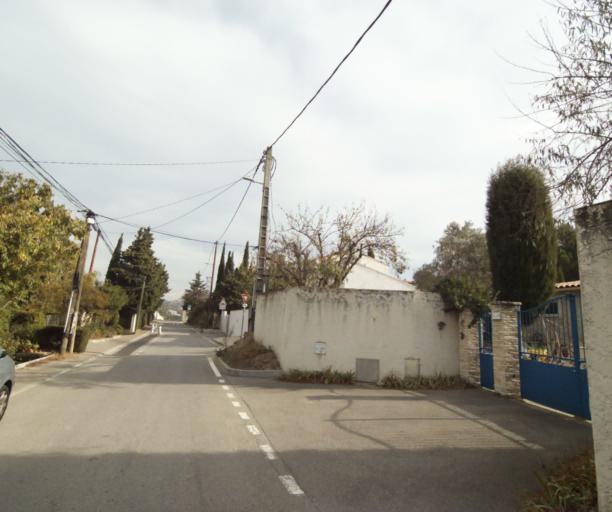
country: FR
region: Provence-Alpes-Cote d'Azur
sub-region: Departement des Bouches-du-Rhone
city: Le Rove
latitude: 43.3659
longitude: 5.2451
